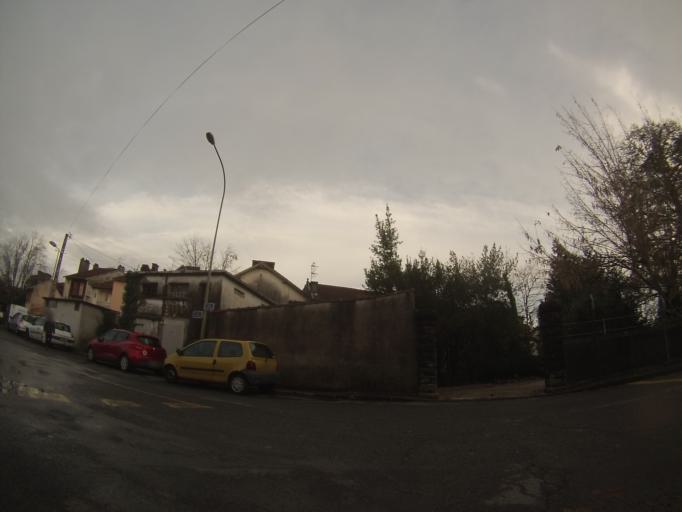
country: FR
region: Aquitaine
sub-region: Departement des Pyrenees-Atlantiques
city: Jurancon
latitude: 43.2892
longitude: -0.3785
